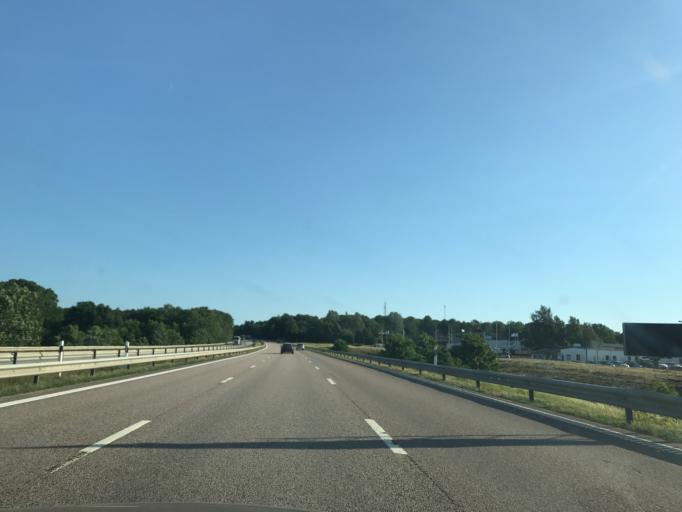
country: SE
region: Skane
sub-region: Angelholms Kommun
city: Munka-Ljungby
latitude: 56.3202
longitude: 12.9141
